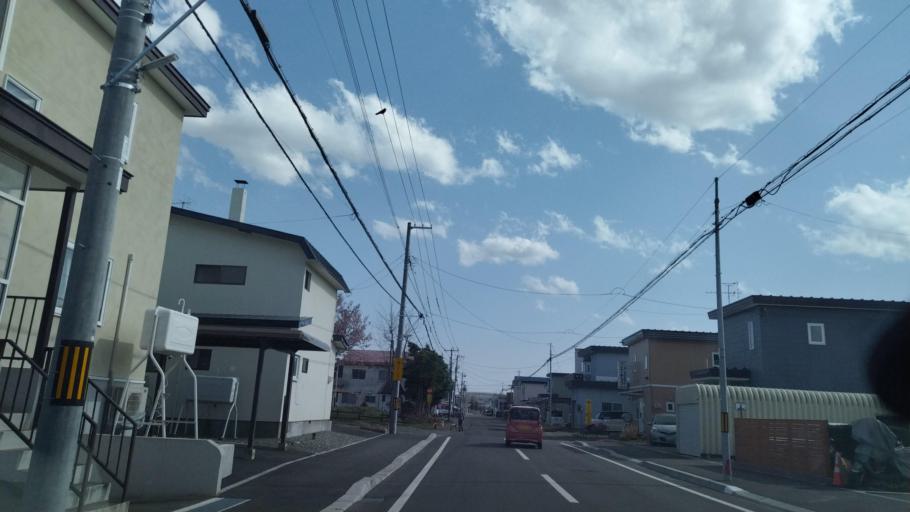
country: JP
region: Hokkaido
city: Obihiro
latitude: 42.9386
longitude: 143.1654
